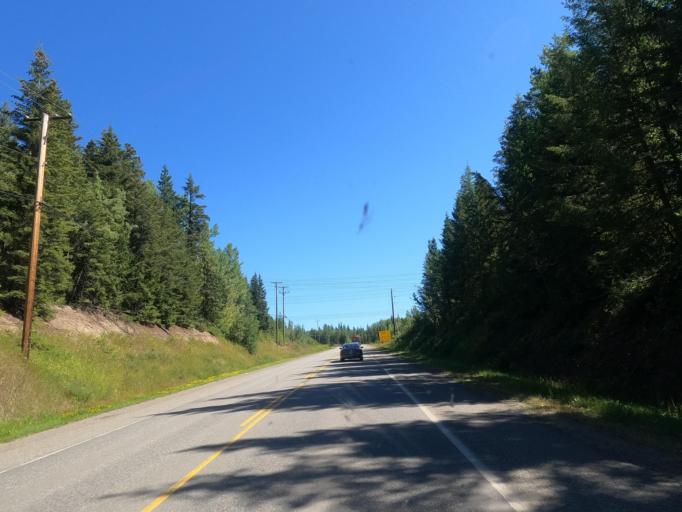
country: CA
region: British Columbia
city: Quesnel
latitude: 53.0504
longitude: -122.4573
